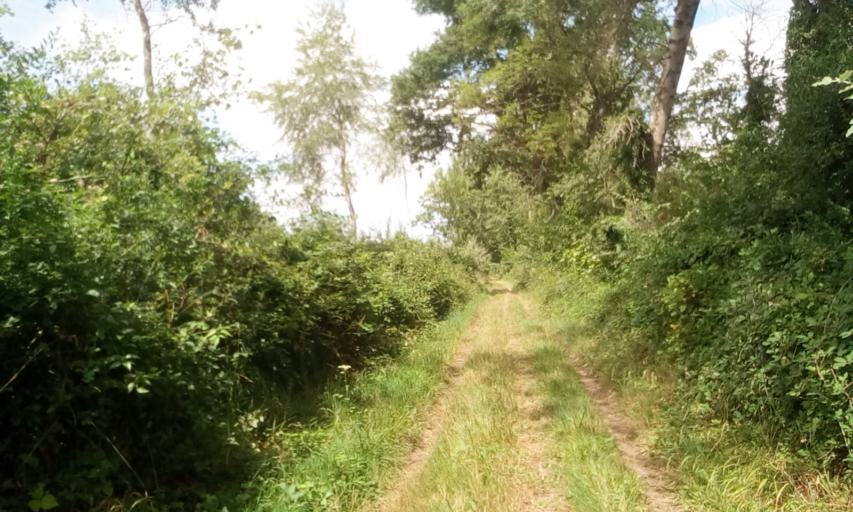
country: FR
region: Lower Normandy
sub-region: Departement du Calvados
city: Bellengreville
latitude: 49.1524
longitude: -0.2056
